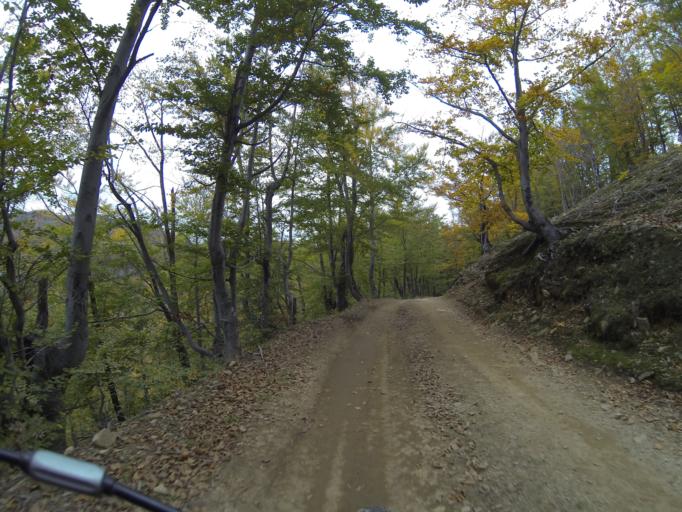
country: RO
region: Gorj
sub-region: Comuna Tismana
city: Sohodol
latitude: 45.0720
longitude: 22.8623
